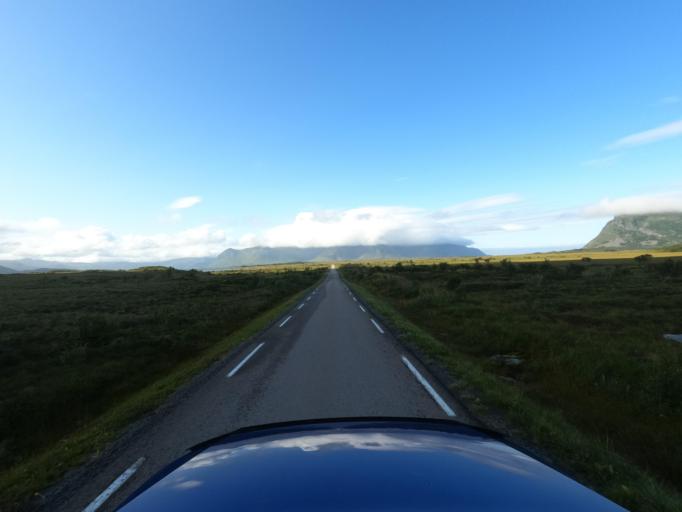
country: NO
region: Nordland
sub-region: Vagan
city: Kabelvag
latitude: 68.3072
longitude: 14.1633
